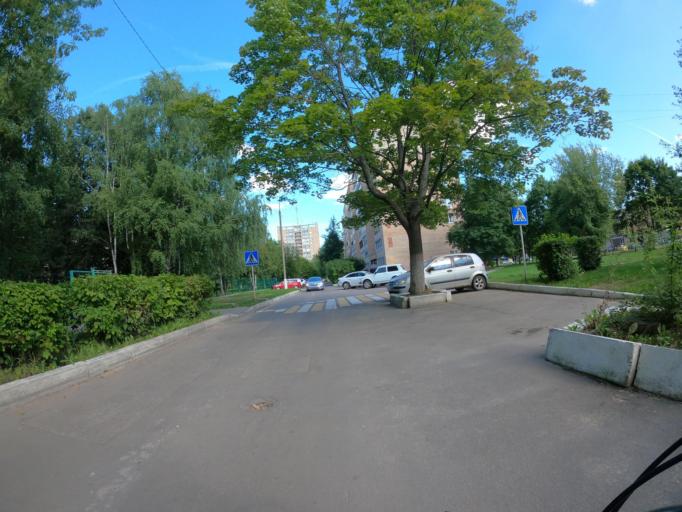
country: RU
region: Moskovskaya
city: Stupino
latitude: 54.8855
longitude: 38.0551
